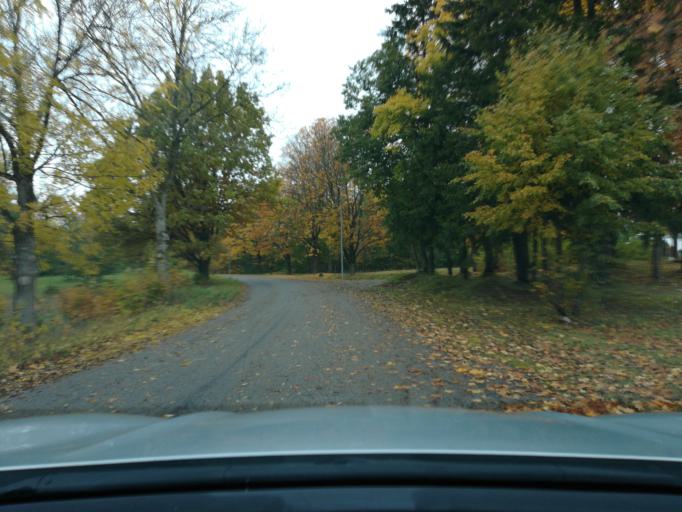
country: EE
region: Ida-Virumaa
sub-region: Johvi vald
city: Johvi
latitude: 59.1943
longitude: 27.5416
